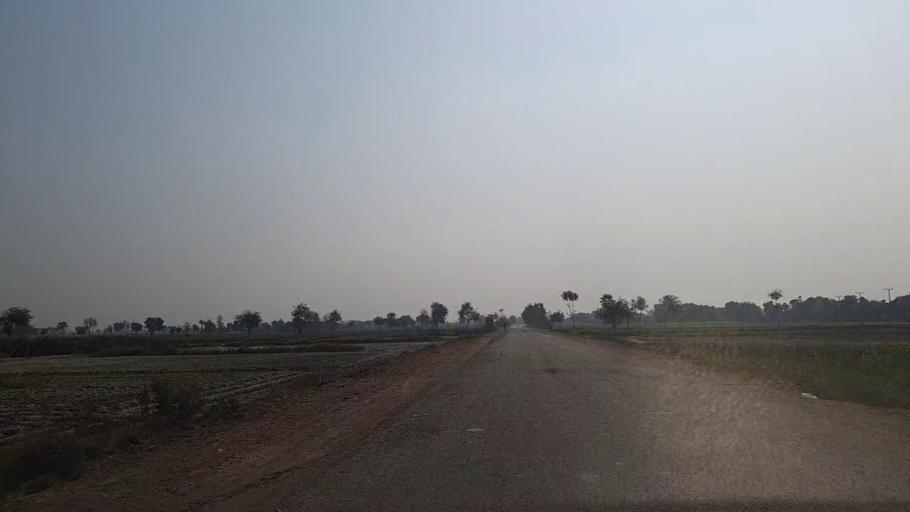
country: PK
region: Sindh
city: Jam Sahib
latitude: 26.3456
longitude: 68.5343
